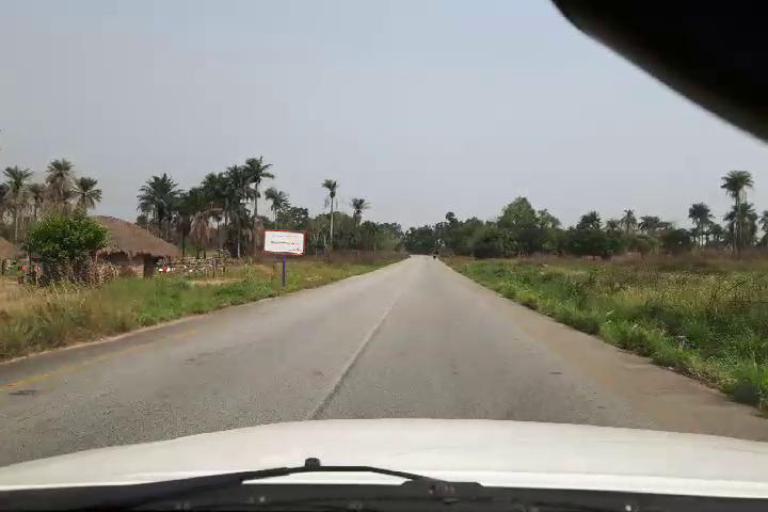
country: SL
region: Southern Province
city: Largo
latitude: 8.3097
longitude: -12.2133
